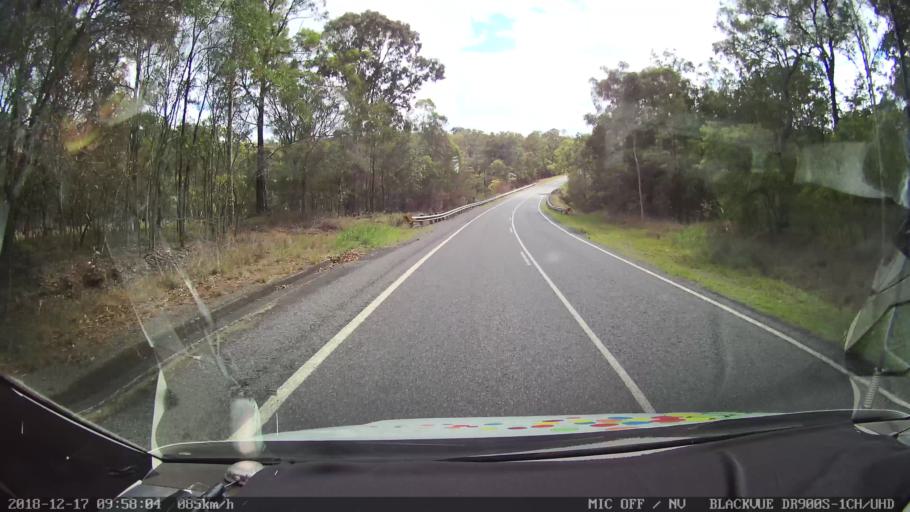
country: AU
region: New South Wales
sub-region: Tenterfield Municipality
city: Carrolls Creek
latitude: -28.9215
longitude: 152.4044
